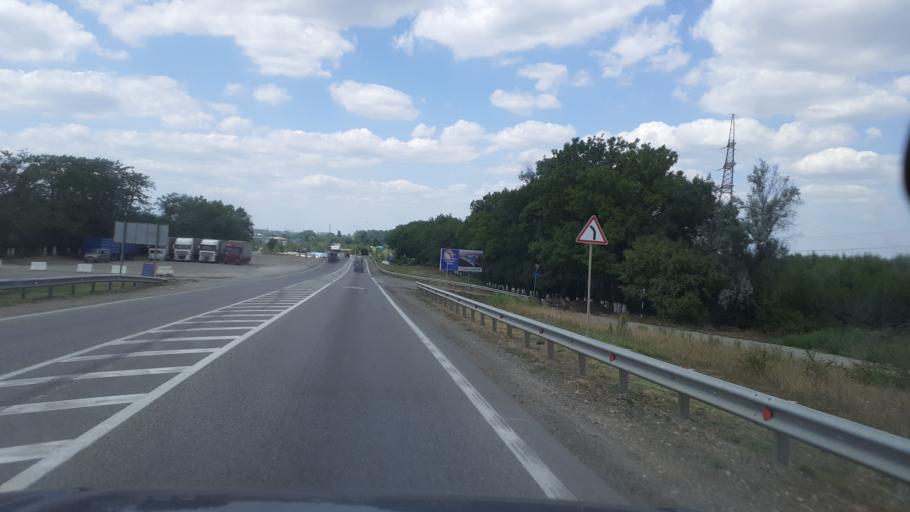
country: RU
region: Krasnodarskiy
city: Il'skiy
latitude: 44.8523
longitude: 38.5969
